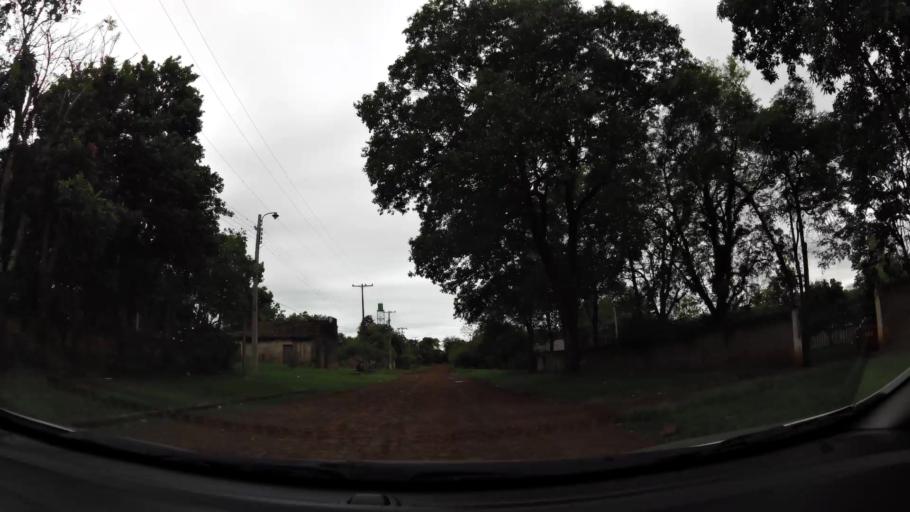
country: PY
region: Alto Parana
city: Ciudad del Este
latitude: -25.4386
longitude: -54.6400
